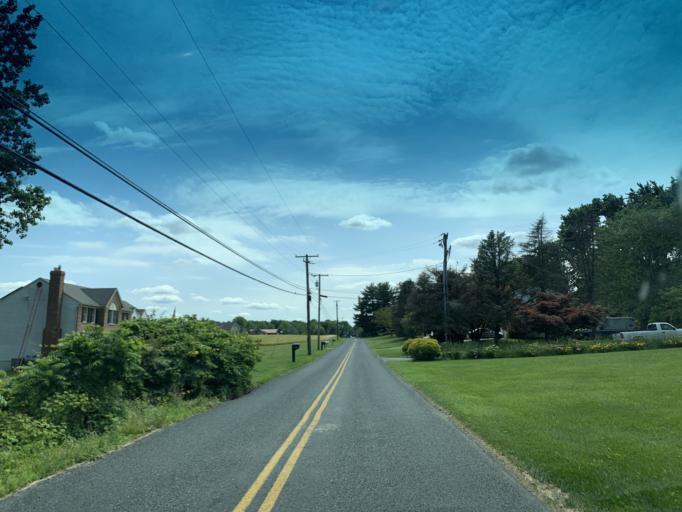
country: US
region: Maryland
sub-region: Harford County
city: Jarrettsville
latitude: 39.6362
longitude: -76.4565
